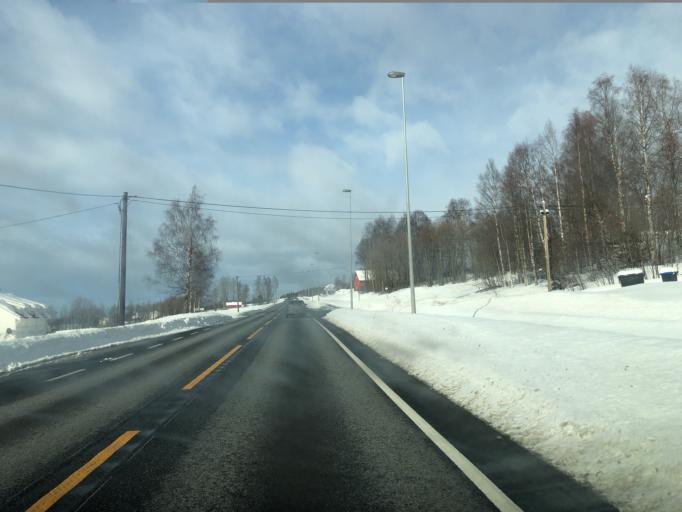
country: NO
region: Oppland
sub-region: Vestre Toten
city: Reinsvoll
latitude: 60.5435
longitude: 10.6580
